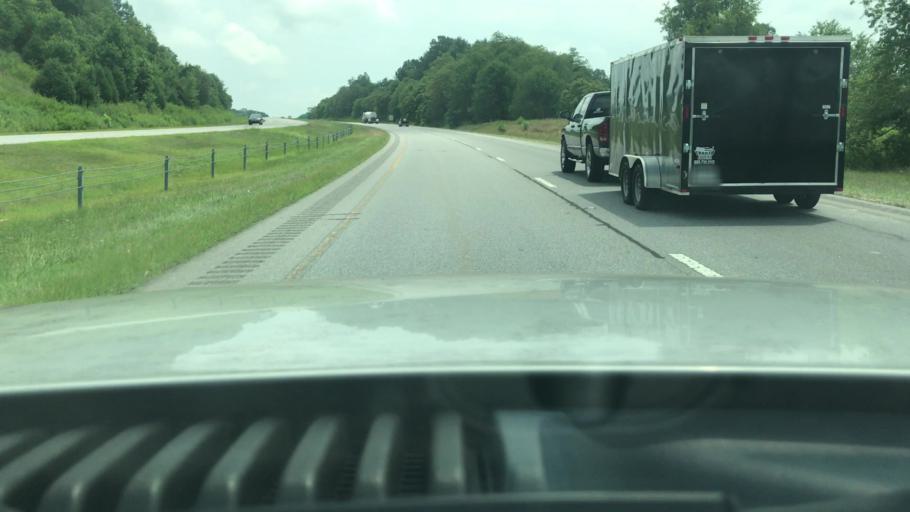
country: US
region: North Carolina
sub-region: Yadkin County
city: Jonesville
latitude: 36.1409
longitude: -80.8893
